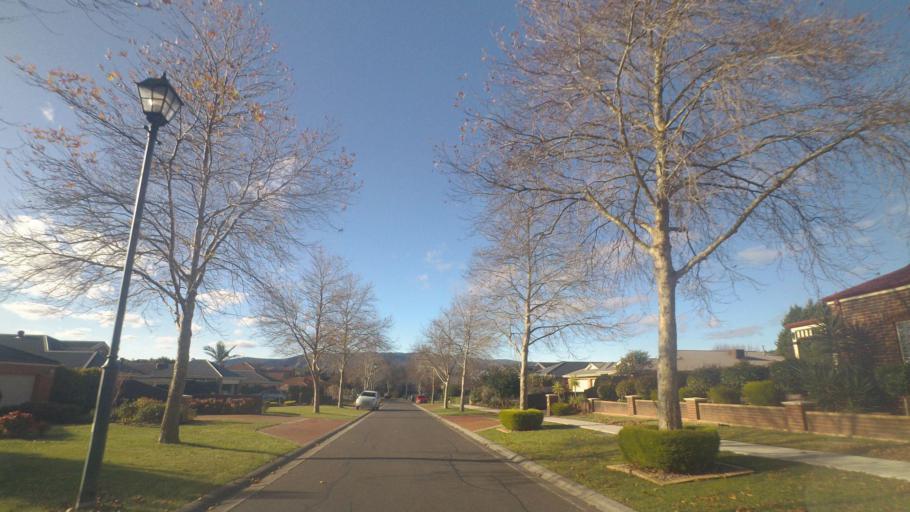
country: AU
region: Victoria
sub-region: Yarra Ranges
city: Lysterfield
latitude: -37.9191
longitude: 145.2827
